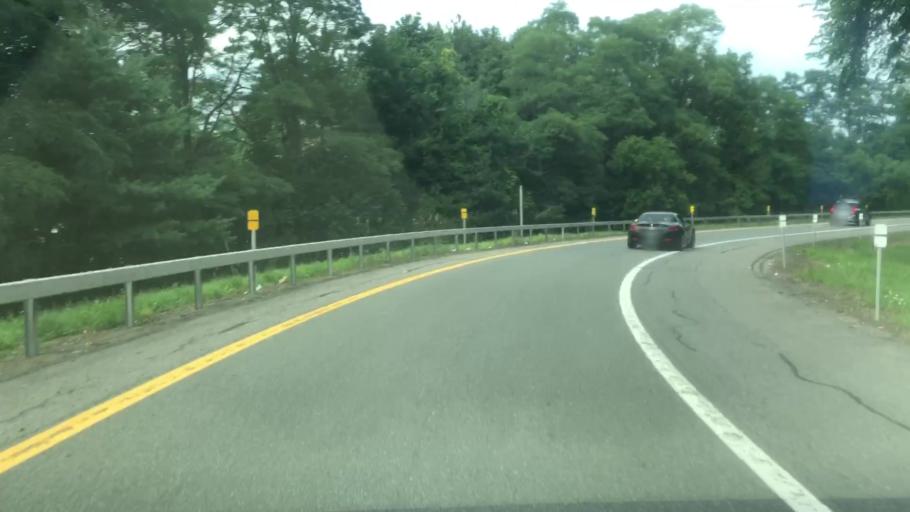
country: US
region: New York
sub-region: Schenectady County
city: Schenectady
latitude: 42.7822
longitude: -73.9251
